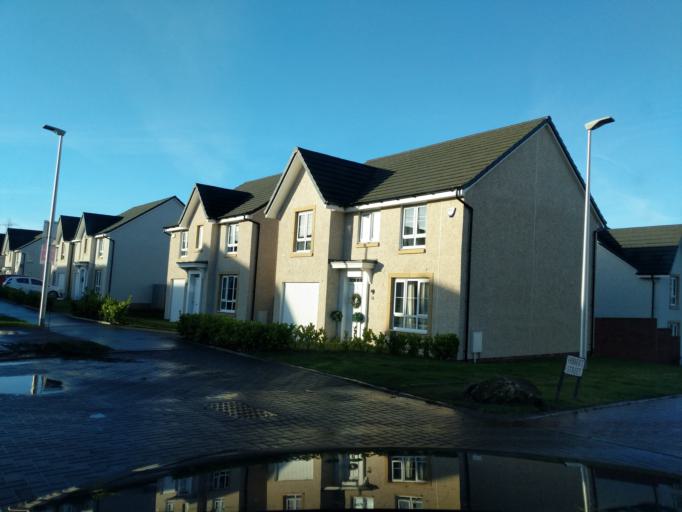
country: GB
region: Scotland
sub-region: Midlothian
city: Loanhead
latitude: 55.8936
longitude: -3.1559
